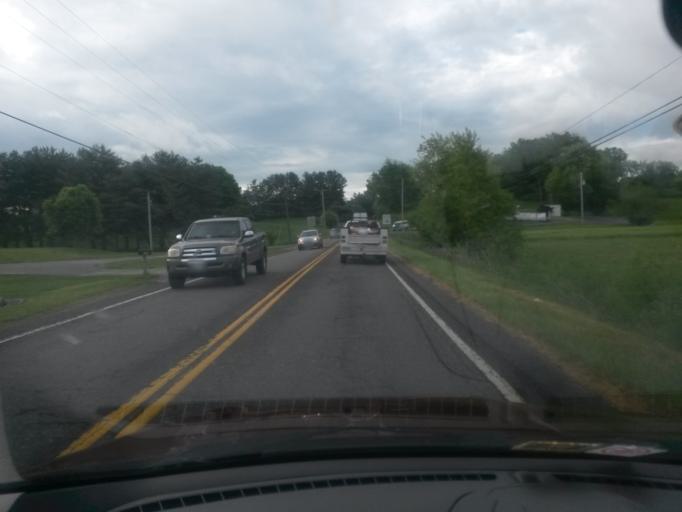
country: US
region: Virginia
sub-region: Montgomery County
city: Christiansburg
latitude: 37.0701
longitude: -80.4431
